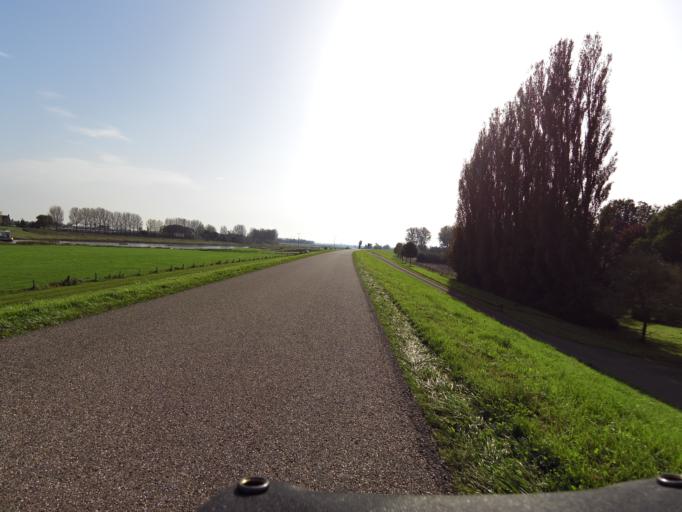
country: NL
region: Gelderland
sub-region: Gemeente Duiven
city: Duiven
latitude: 51.8941
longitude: 6.0209
